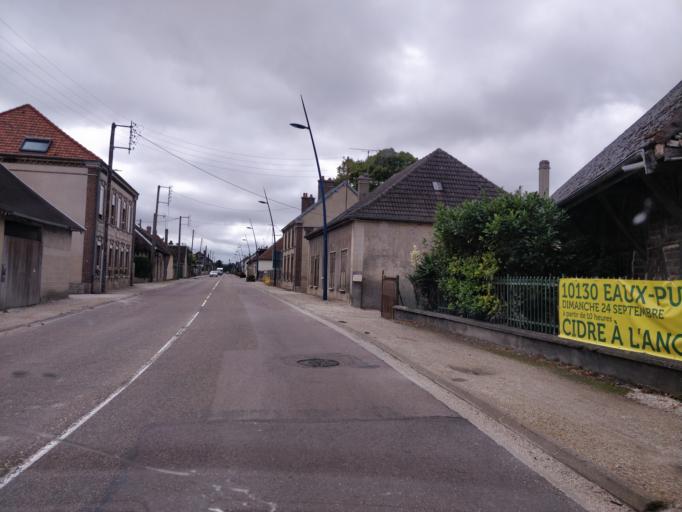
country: FR
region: Champagne-Ardenne
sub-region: Departement de l'Aube
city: Saint-Germain
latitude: 48.2603
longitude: 4.0325
